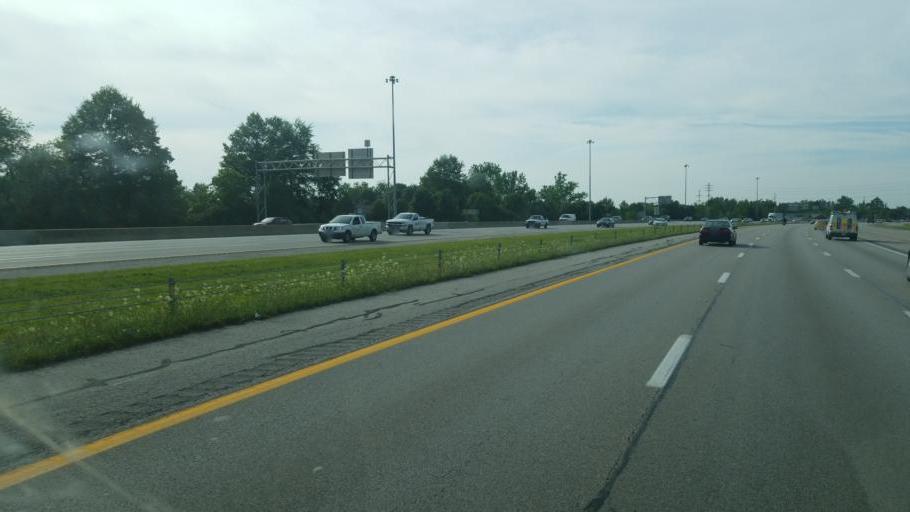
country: US
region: Ohio
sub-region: Franklin County
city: Whitehall
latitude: 39.9806
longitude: -82.8545
